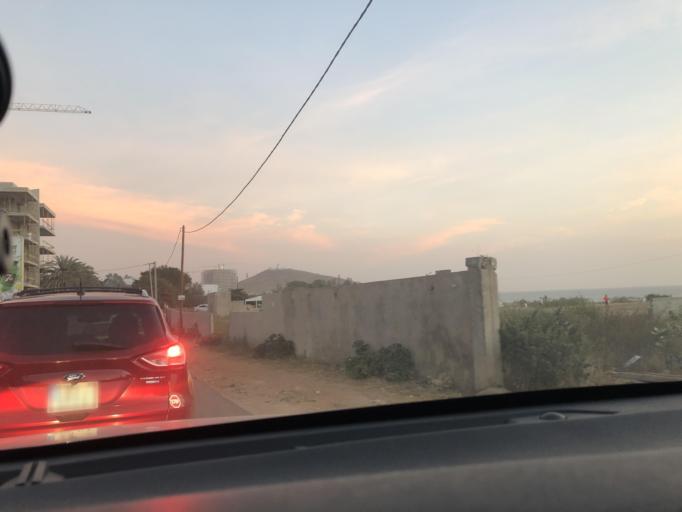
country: SN
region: Dakar
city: Mermoz Boabab
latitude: 14.7356
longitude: -17.5122
